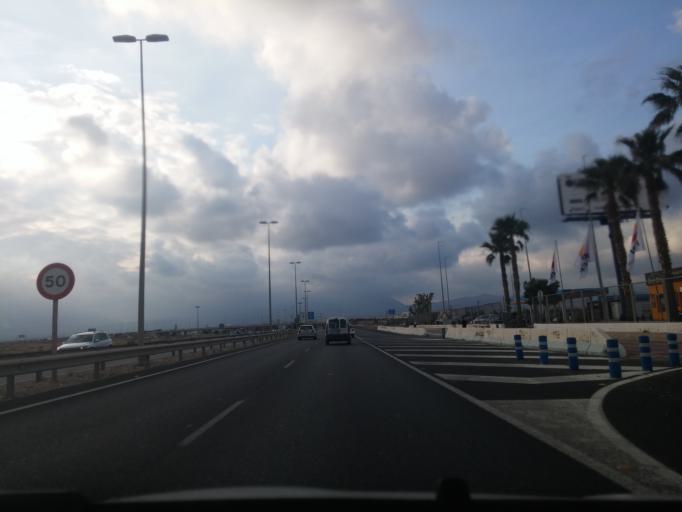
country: ES
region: Valencia
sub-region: Provincia de Alicante
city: San Vicent del Raspeig
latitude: 38.3757
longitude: -0.5091
